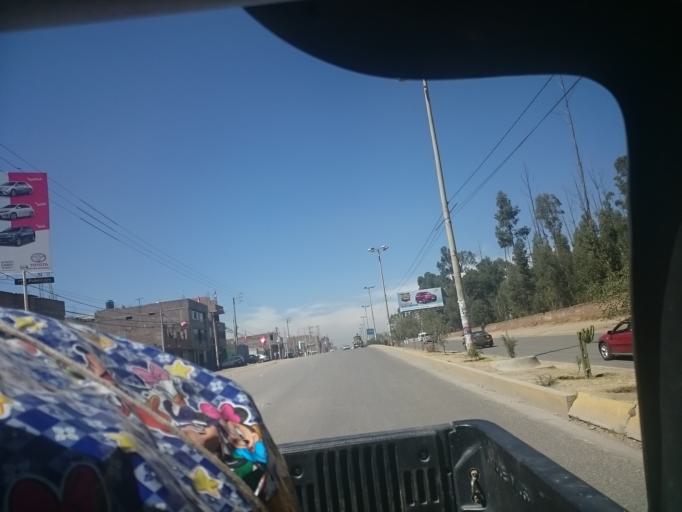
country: PE
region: Junin
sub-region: Provincia de Huancayo
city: Pilcomay
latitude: -12.0354
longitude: -75.2312
